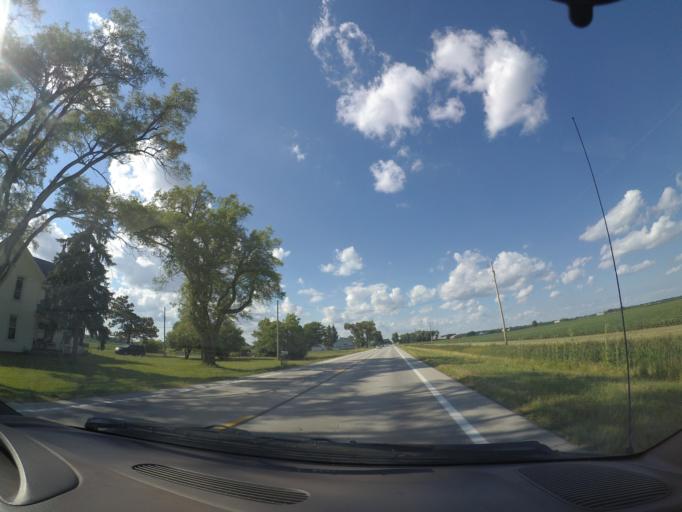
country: US
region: Ohio
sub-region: Sandusky County
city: Woodville
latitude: 41.4575
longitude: -83.4151
